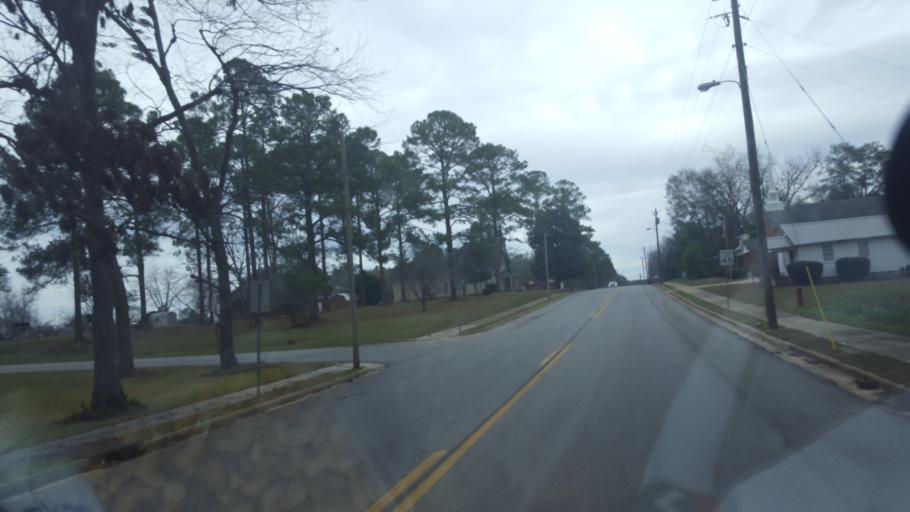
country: US
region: Georgia
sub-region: Wilcox County
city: Rochelle
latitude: 31.8080
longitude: -83.4854
